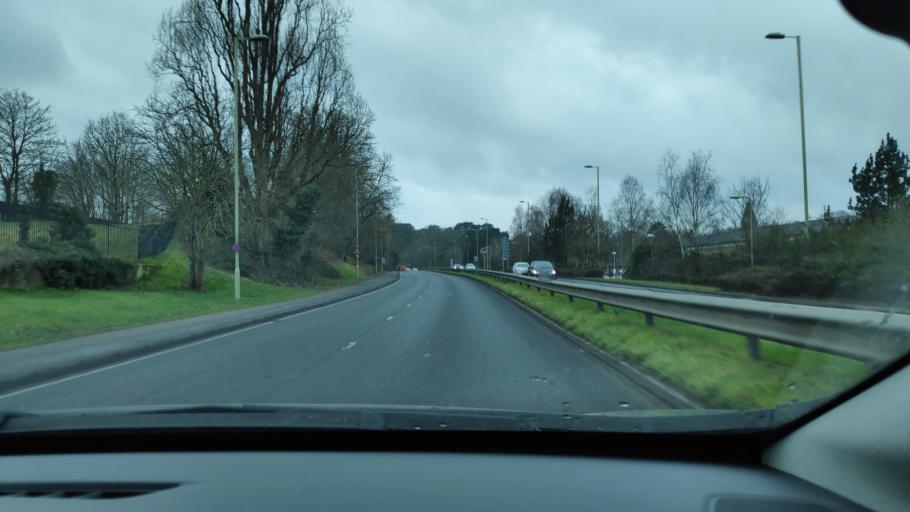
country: GB
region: England
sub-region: Hampshire
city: Aldershot
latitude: 51.2500
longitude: -0.7739
